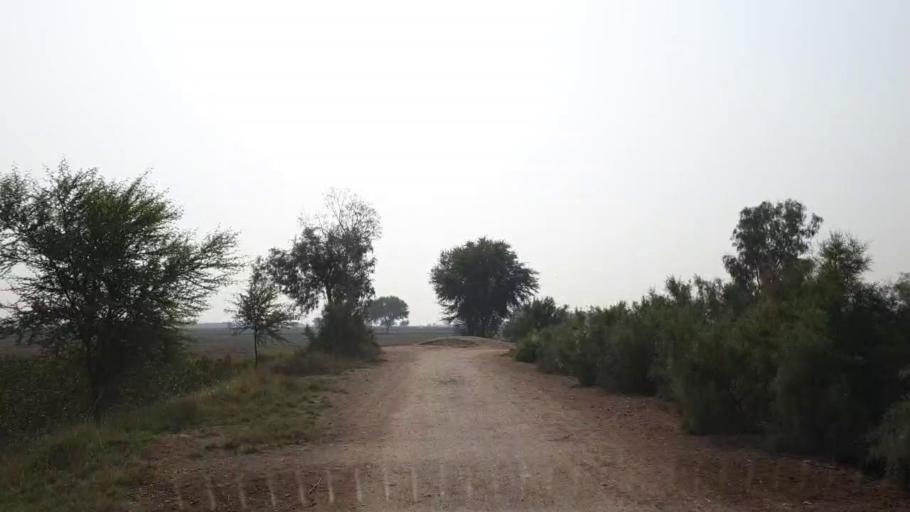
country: PK
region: Sindh
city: Bhan
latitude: 26.4650
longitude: 67.7393
